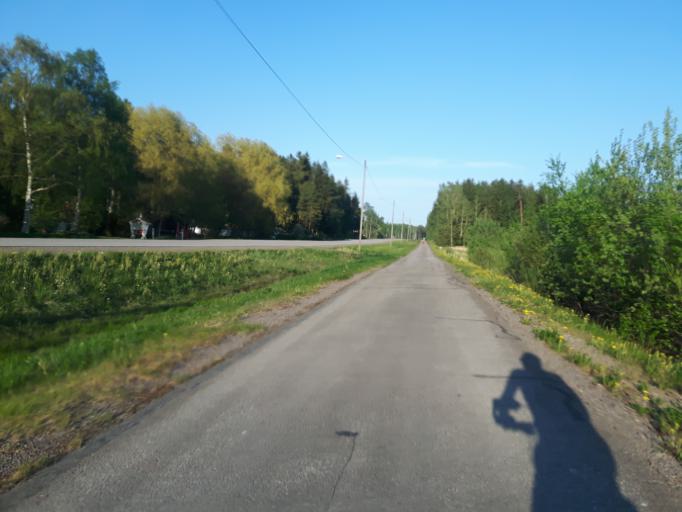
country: FI
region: Uusimaa
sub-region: Loviisa
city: Lovisa
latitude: 60.4571
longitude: 26.1307
